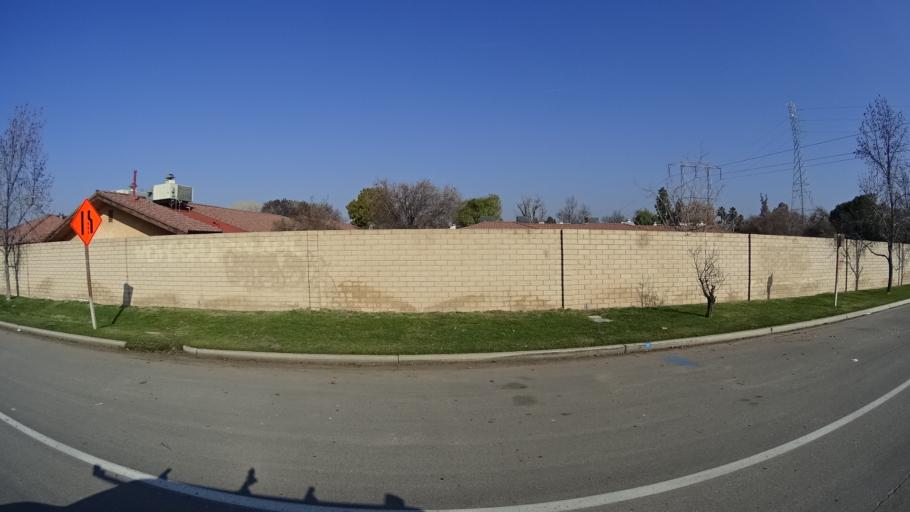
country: US
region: California
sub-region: Kern County
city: Oildale
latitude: 35.4052
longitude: -119.0075
